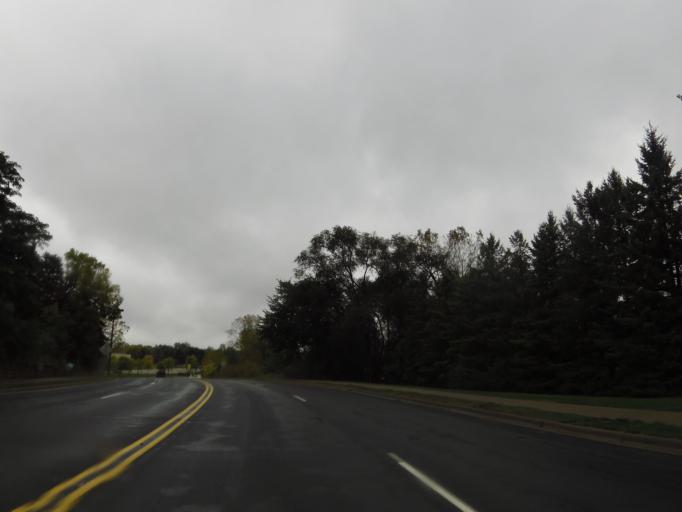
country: US
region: Minnesota
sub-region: Dakota County
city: Inver Grove Heights
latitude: 44.8302
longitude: -93.0421
